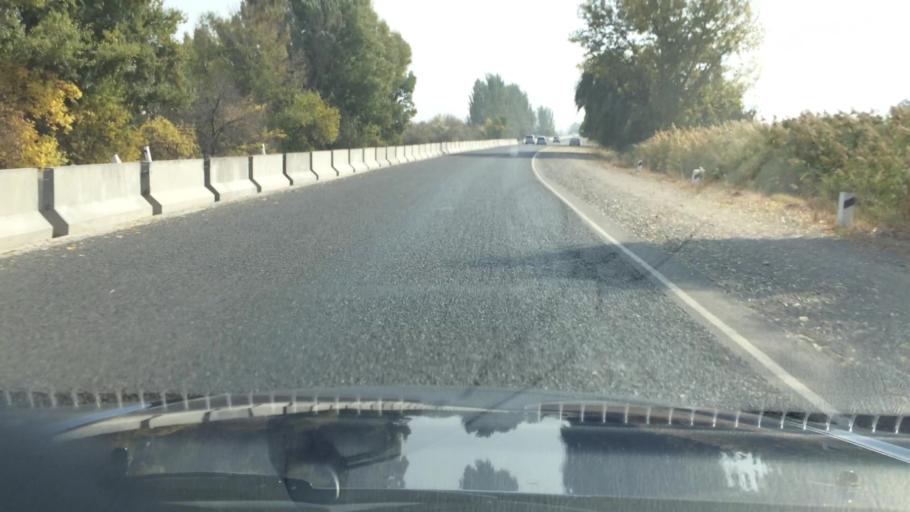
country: KG
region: Chuy
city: Kant
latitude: 42.9748
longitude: 74.8942
